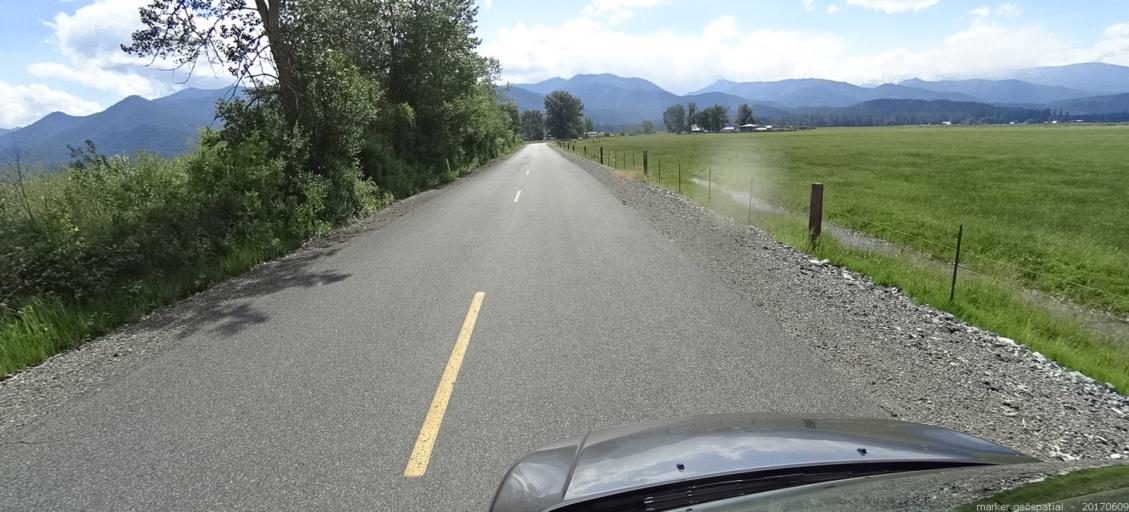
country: US
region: California
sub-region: Siskiyou County
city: Yreka
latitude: 41.5137
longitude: -122.8777
